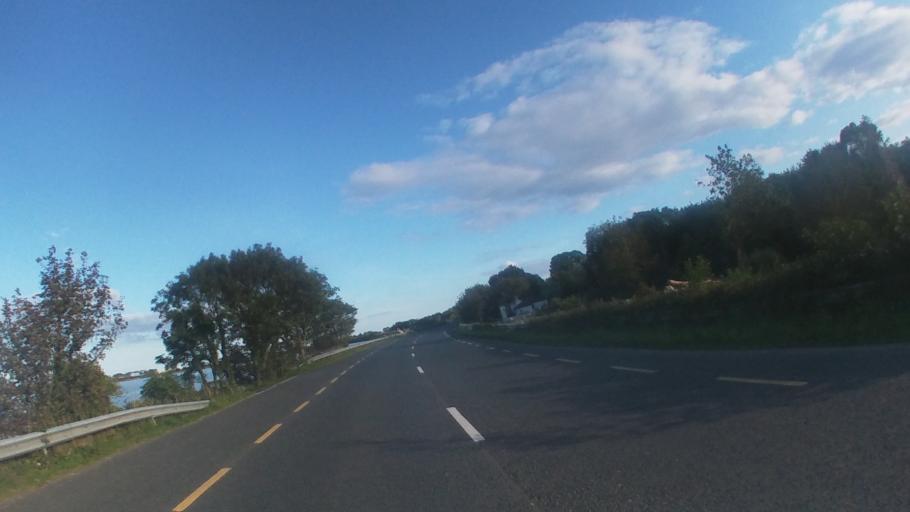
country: IE
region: Leinster
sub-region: Lu
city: Carlingford
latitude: 54.0326
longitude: -6.1603
